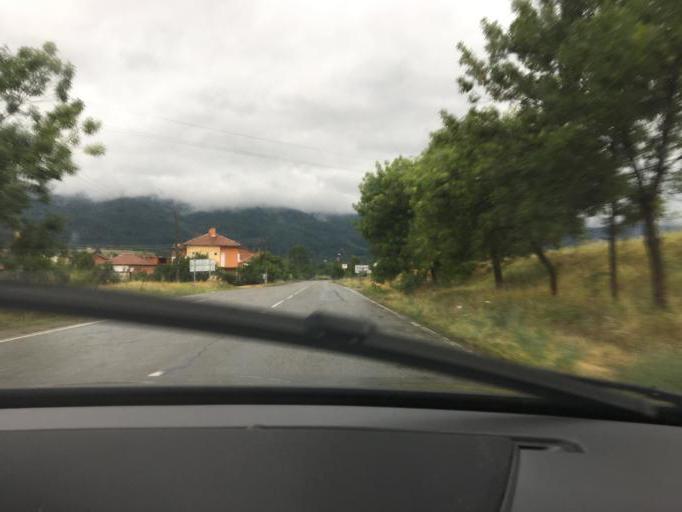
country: BG
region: Kyustendil
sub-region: Obshtina Kyustendil
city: Kyustendil
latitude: 42.2762
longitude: 22.6555
